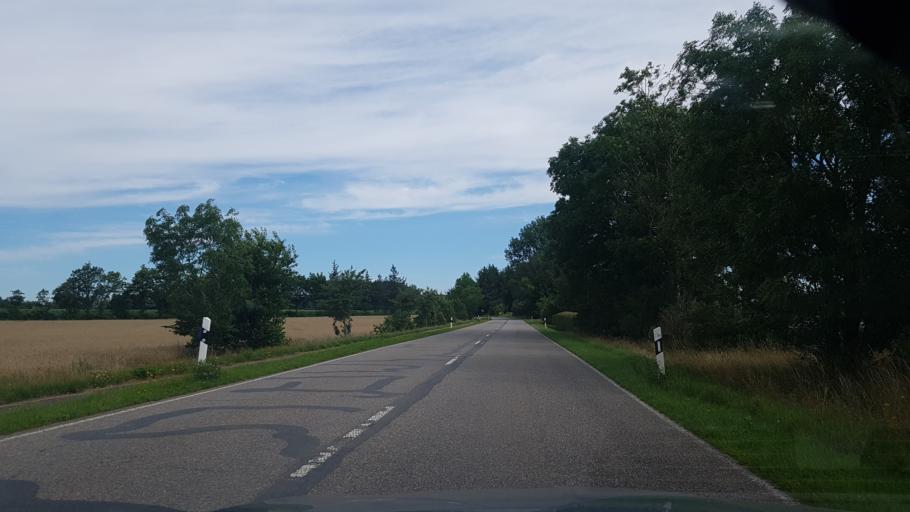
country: DE
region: Schleswig-Holstein
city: Ladelund
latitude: 54.8450
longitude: 9.0349
